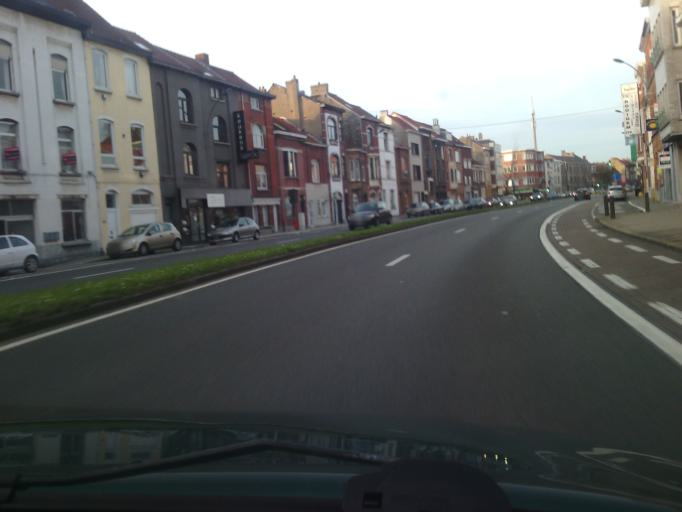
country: BE
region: Flanders
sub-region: Provincie Oost-Vlaanderen
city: Gent
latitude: 51.0576
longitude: 3.6932
